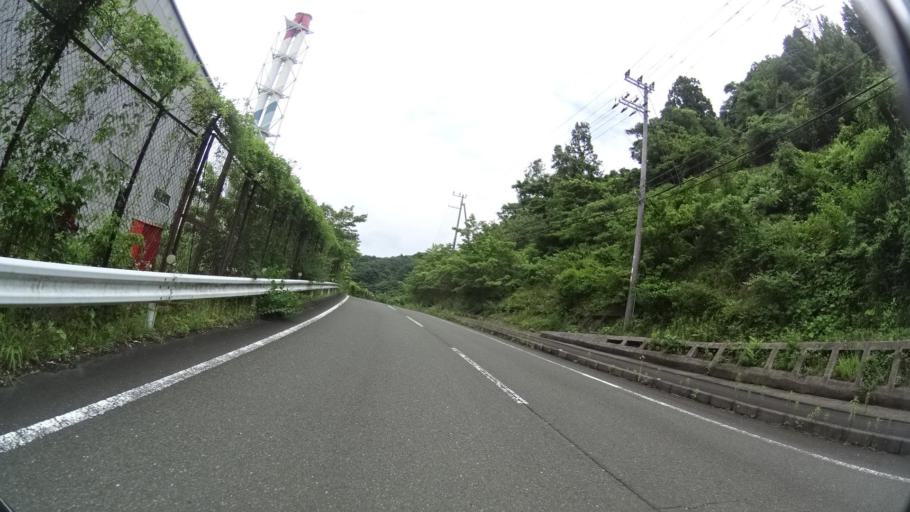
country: JP
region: Kyoto
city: Maizuru
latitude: 35.5261
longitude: 135.3458
